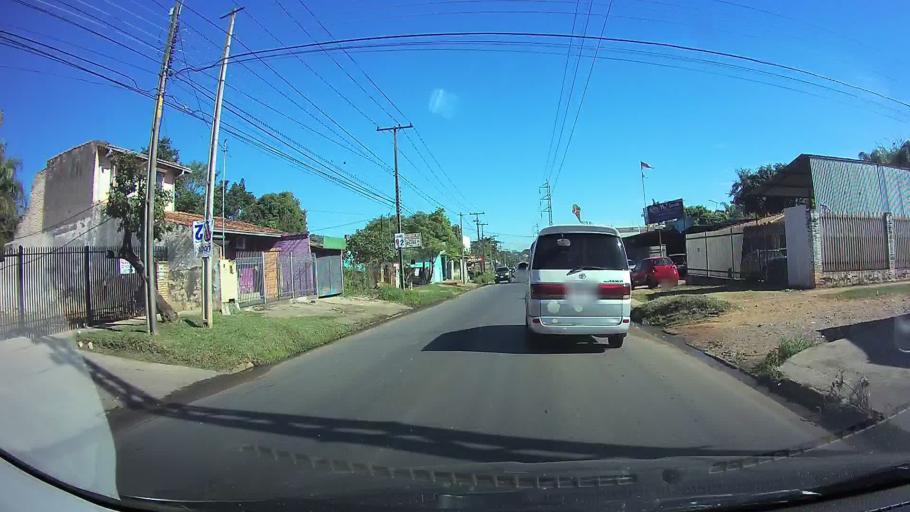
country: PY
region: Central
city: Fernando de la Mora
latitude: -25.3569
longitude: -57.5528
